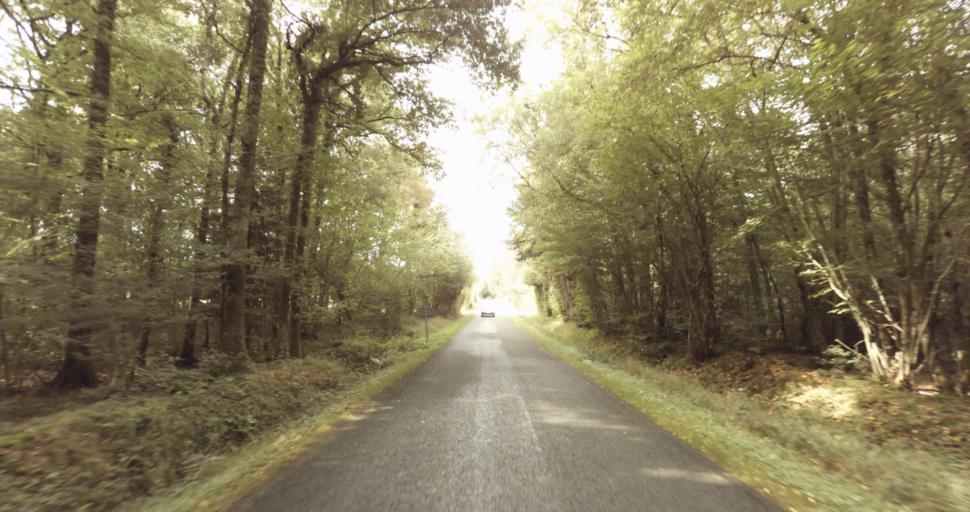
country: FR
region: Lower Normandy
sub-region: Departement de l'Orne
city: Sainte-Gauburge-Sainte-Colombe
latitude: 48.7791
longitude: 0.3888
